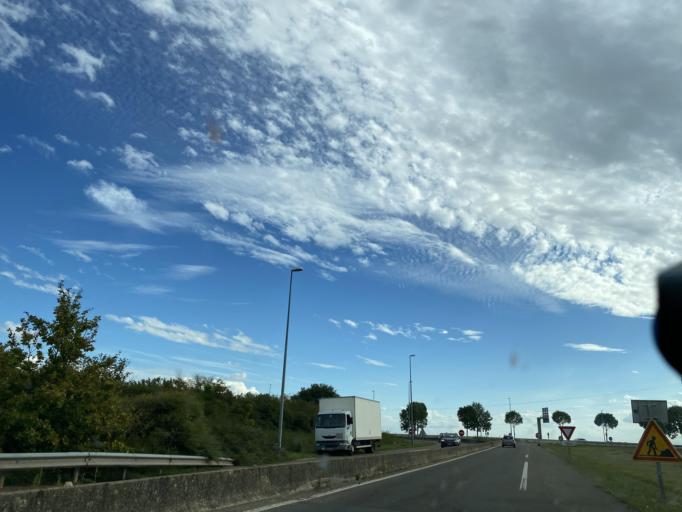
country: FR
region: Centre
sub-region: Departement d'Eure-et-Loir
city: Le Coudray
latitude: 48.4171
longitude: 1.5014
